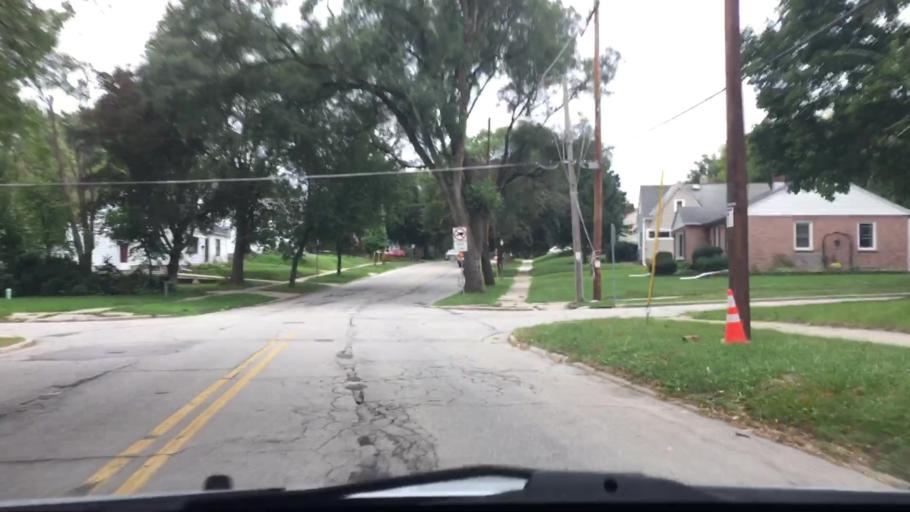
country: US
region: Wisconsin
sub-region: Waukesha County
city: Waukesha
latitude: 43.0160
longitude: -88.2130
